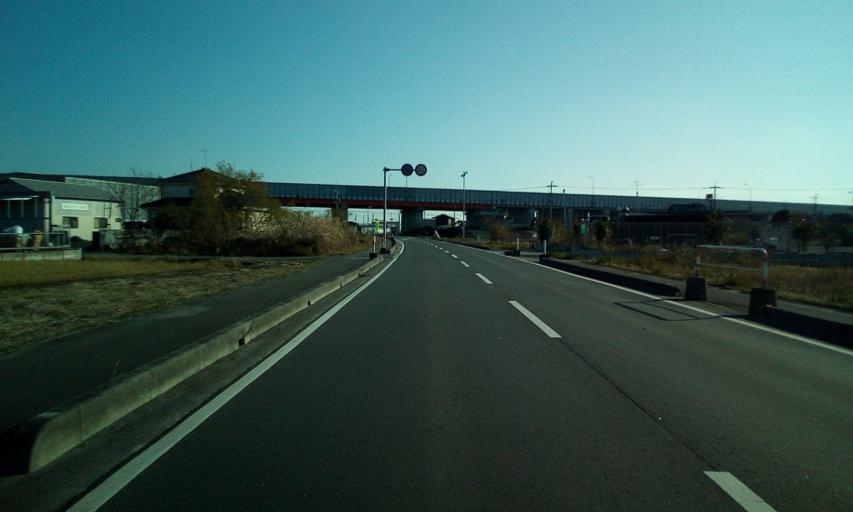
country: JP
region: Chiba
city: Nagareyama
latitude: 35.8755
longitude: 139.8890
